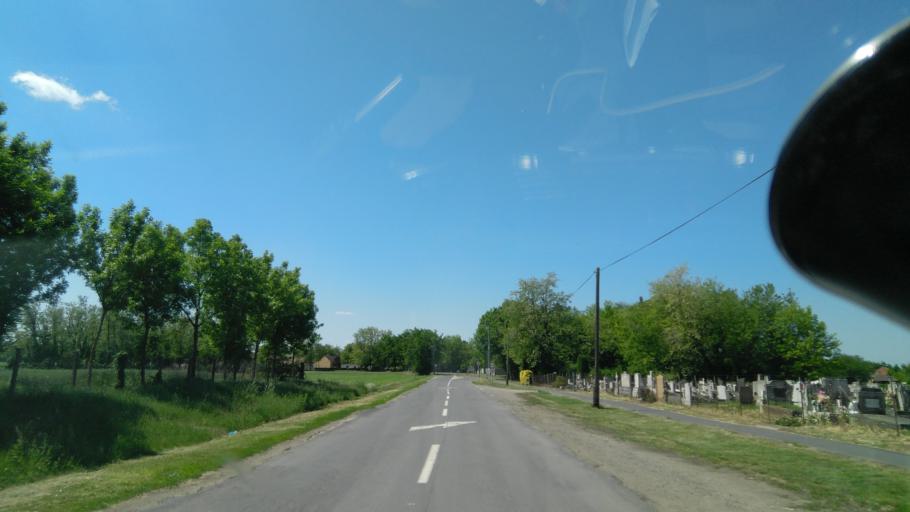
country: HU
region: Bekes
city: Kunagota
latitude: 46.4305
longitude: 21.0608
